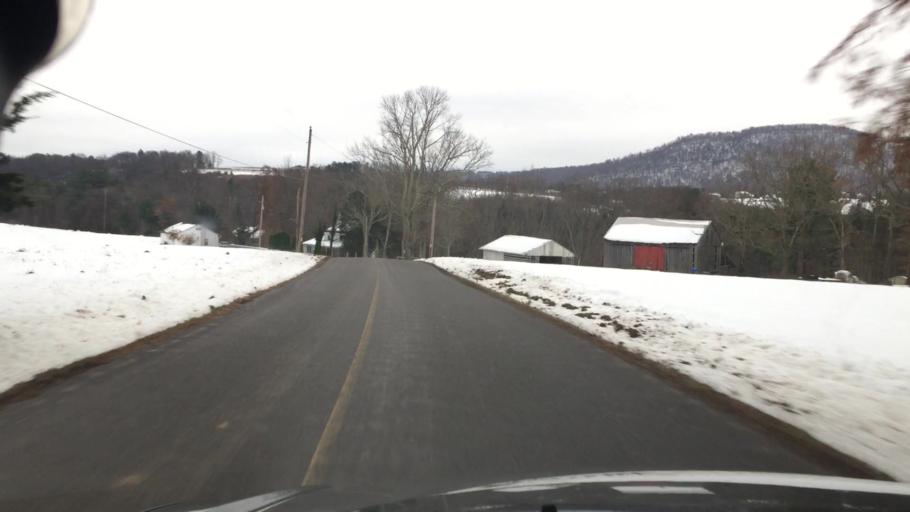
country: US
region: Pennsylvania
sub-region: Luzerne County
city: Conyngham
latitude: 41.0056
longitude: -76.1188
